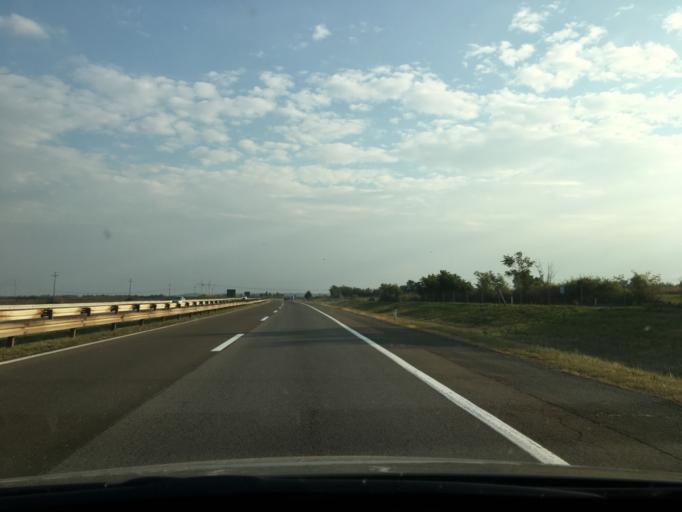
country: RS
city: Lugavcina
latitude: 44.5634
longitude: 20.9814
